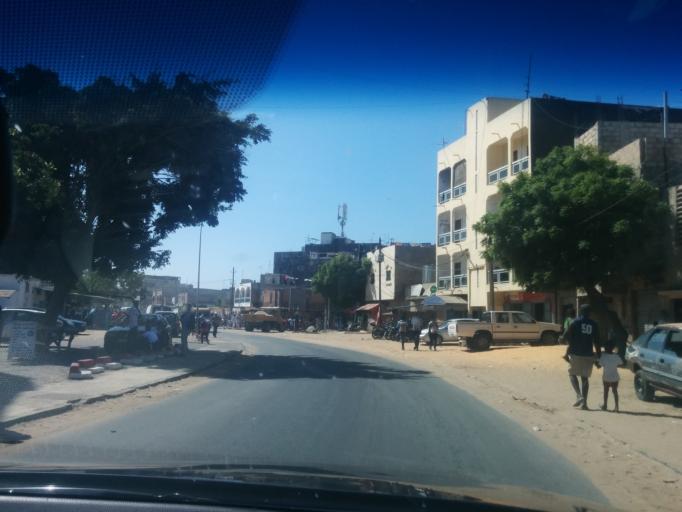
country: SN
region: Dakar
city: Grand Dakar
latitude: 14.7363
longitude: -17.4456
